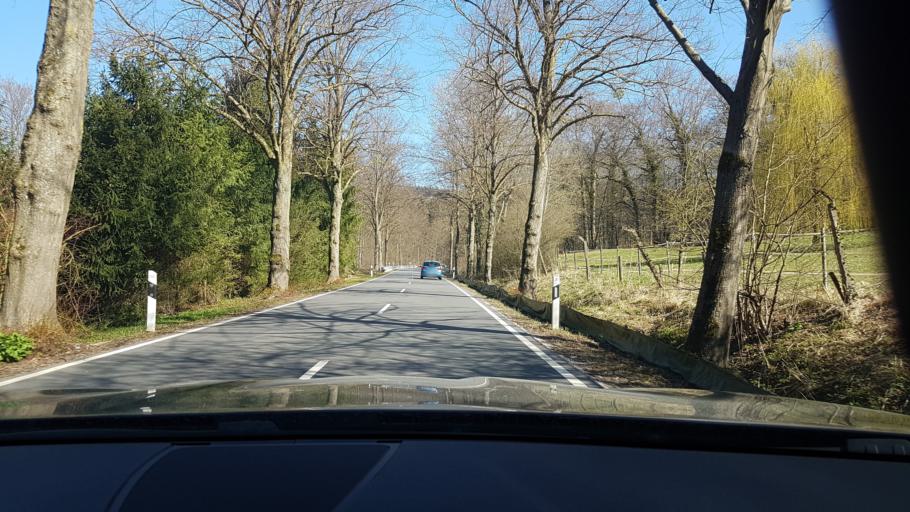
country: DE
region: Lower Saxony
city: Coppenbrugge
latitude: 52.1421
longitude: 9.5737
